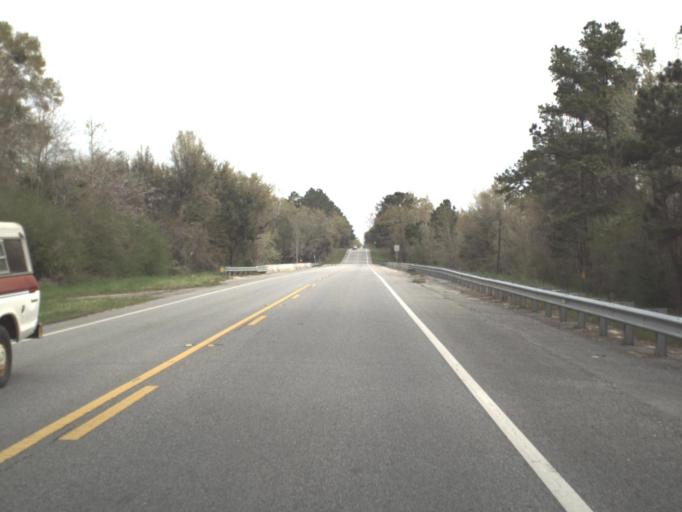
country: US
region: Florida
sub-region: Holmes County
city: Bonifay
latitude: 30.8776
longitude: -85.6621
